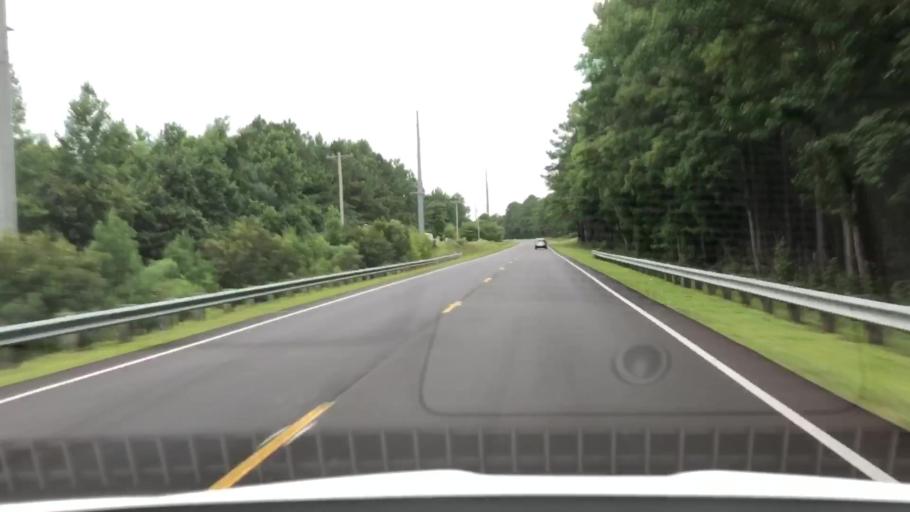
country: US
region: North Carolina
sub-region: Jones County
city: Maysville
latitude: 34.8272
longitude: -77.1563
